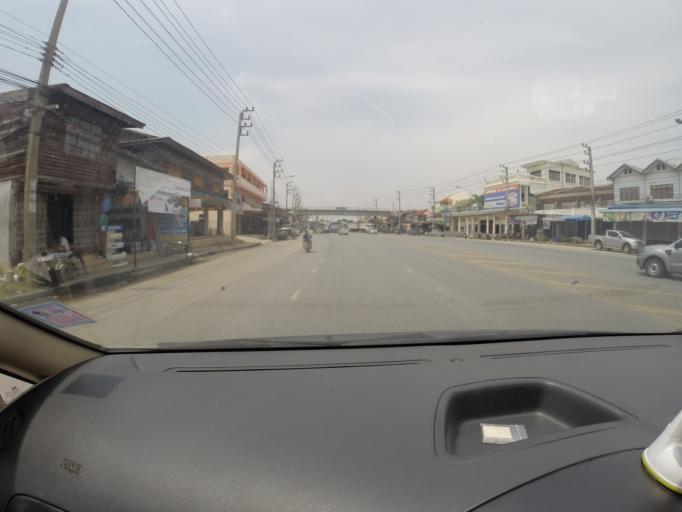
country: TH
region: Chaiyaphum
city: Noen Sa-nga
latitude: 15.6849
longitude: 102.0085
